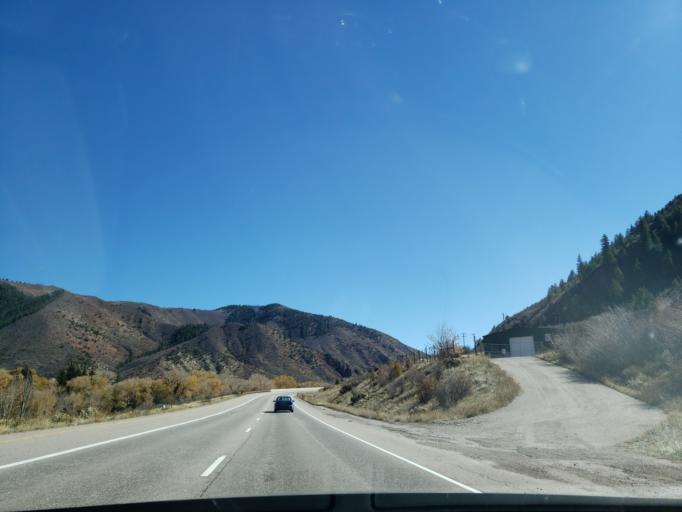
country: US
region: Colorado
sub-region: Eagle County
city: Basalt
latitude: 39.3242
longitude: -106.9498
